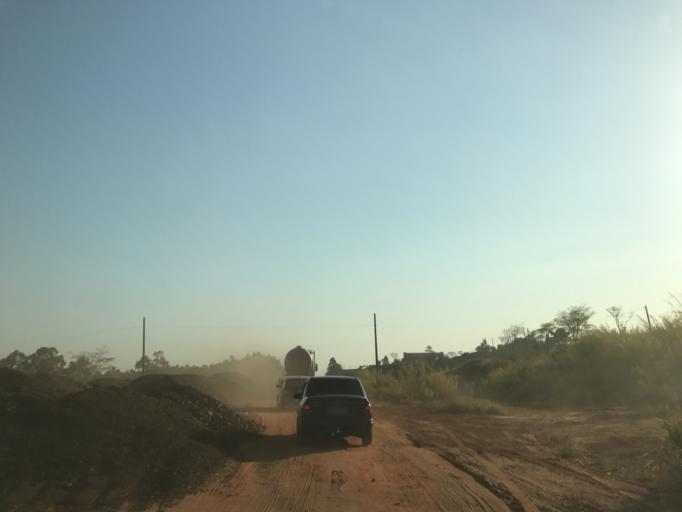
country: BR
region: Sao Paulo
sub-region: Marilia
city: Marilia
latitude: -22.1155
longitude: -49.9282
